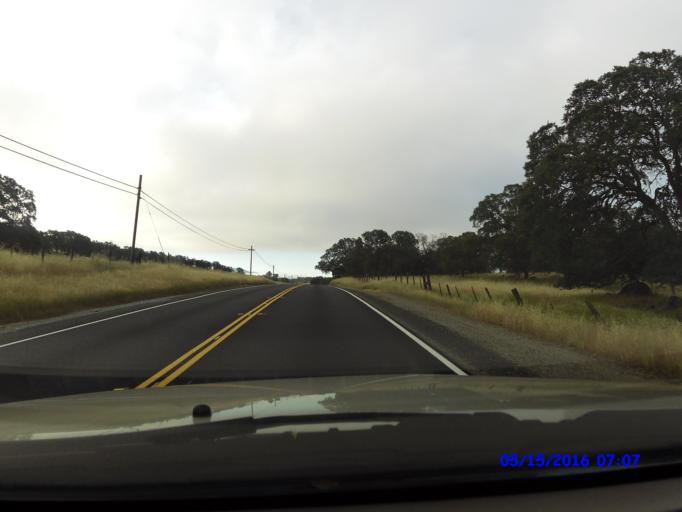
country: US
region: California
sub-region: Tuolumne County
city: Jamestown
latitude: 37.8906
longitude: -120.4450
